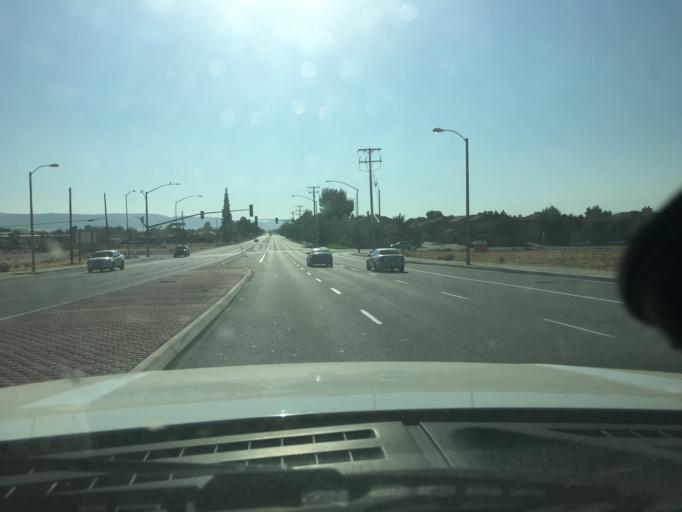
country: US
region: California
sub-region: Los Angeles County
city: Lancaster
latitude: 34.6604
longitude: -118.1554
